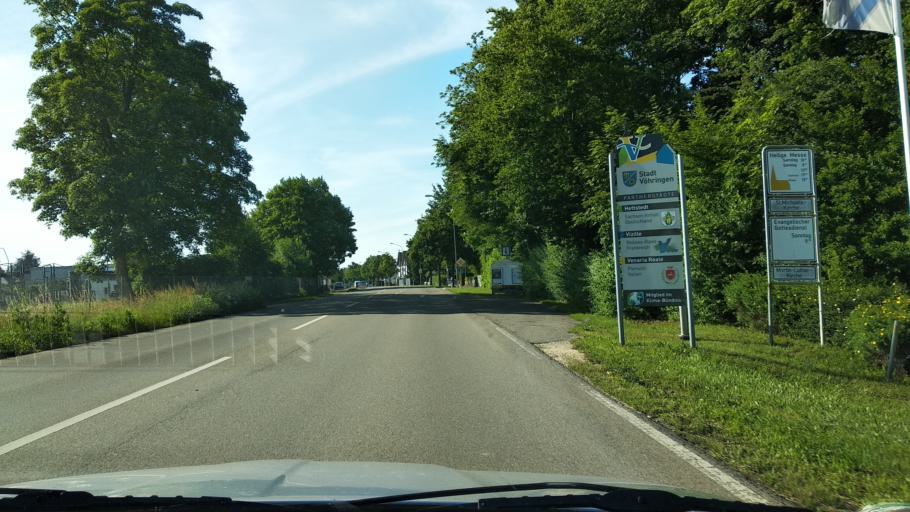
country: DE
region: Bavaria
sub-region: Swabia
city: Vohringen
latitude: 48.2698
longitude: 10.0844
